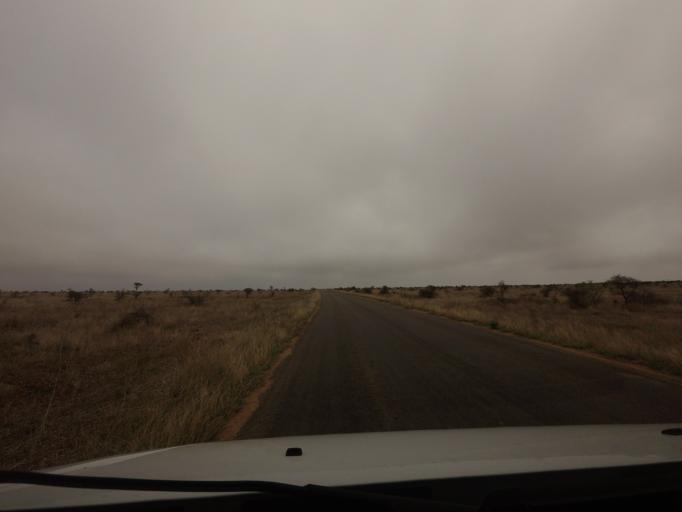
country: ZA
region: Limpopo
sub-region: Mopani District Municipality
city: Phalaborwa
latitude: -24.2238
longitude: 31.7212
